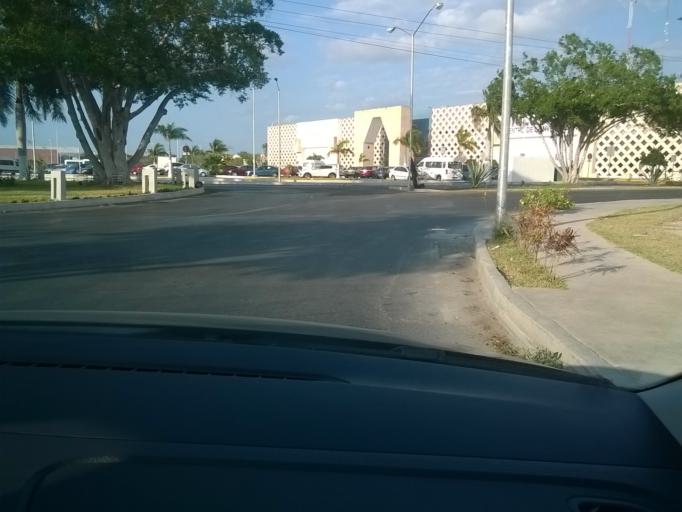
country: MX
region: Yucatan
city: Merida
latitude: 21.0324
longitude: -89.6311
